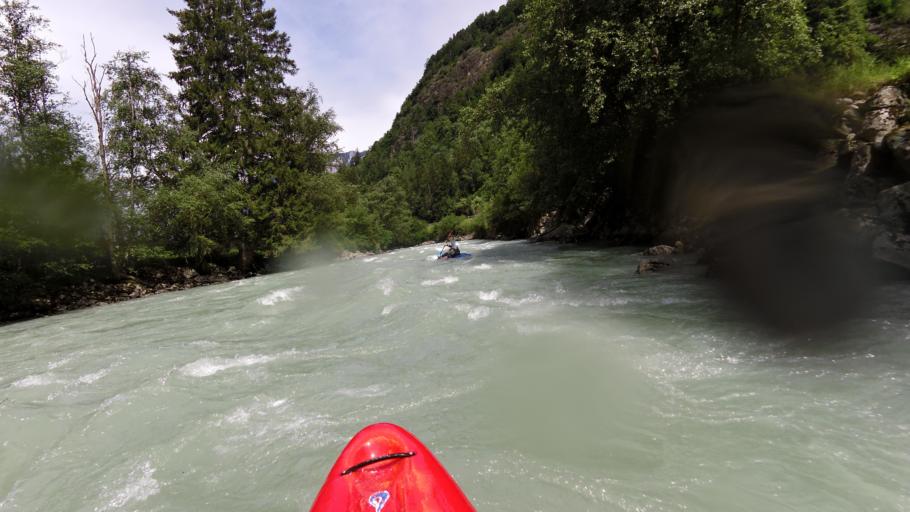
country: AT
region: Tyrol
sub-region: Politischer Bezirk Imst
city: Sautens
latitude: 47.2058
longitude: 10.8794
